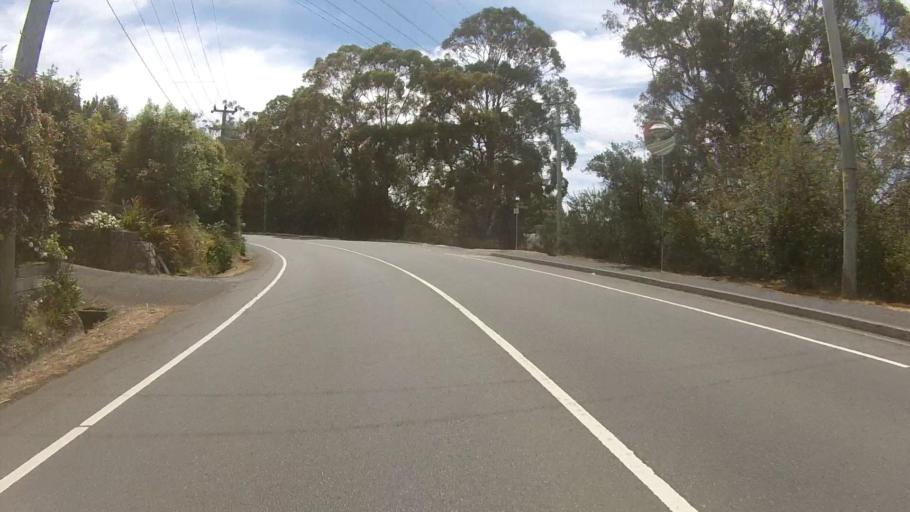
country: AU
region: Tasmania
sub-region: Kingborough
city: Taroona
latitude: -42.9405
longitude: 147.3530
